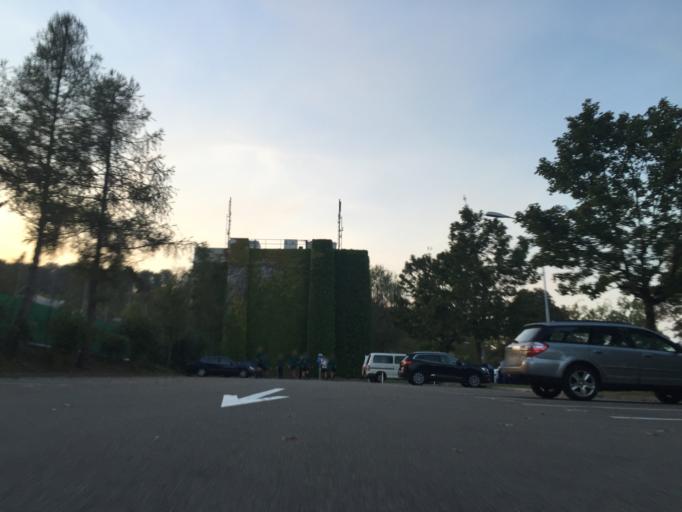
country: CH
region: Zurich
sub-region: Bezirk Zuerich
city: Zuerich (Kreis 7)
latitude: 47.3829
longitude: 8.5750
